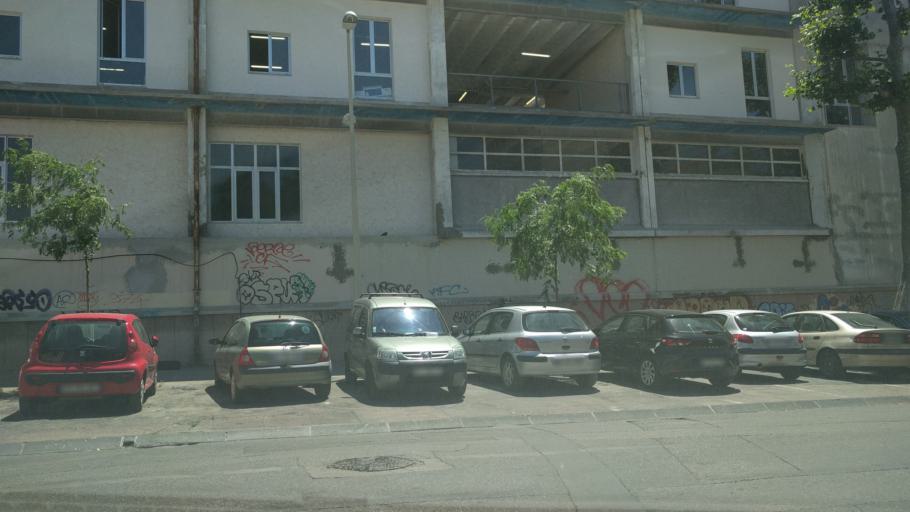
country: FR
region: Provence-Alpes-Cote d'Azur
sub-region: Departement des Bouches-du-Rhone
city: Marseille 01
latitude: 43.3111
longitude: 5.3894
